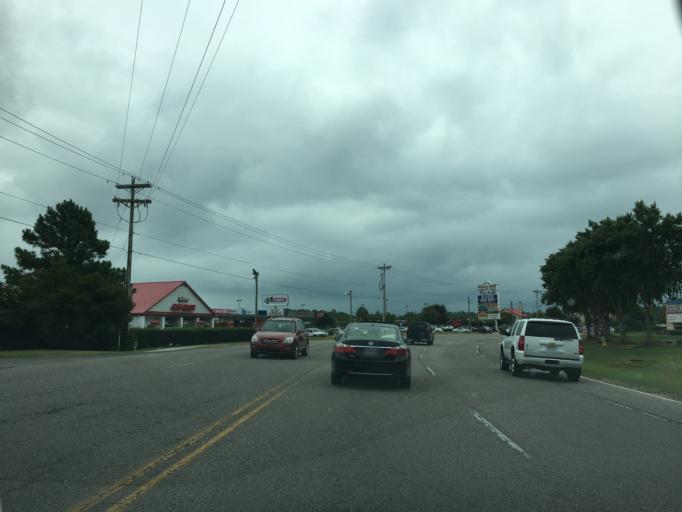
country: US
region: South Carolina
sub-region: Horry County
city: North Myrtle Beach
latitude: 33.7860
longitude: -78.7714
